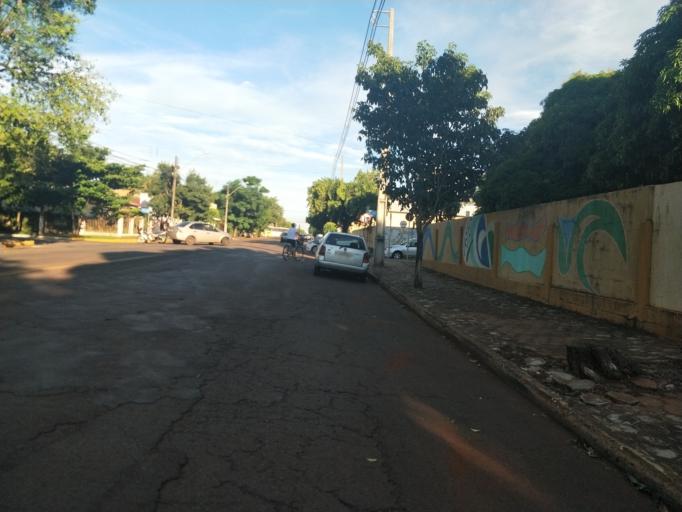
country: BR
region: Parana
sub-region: Marechal Candido Rondon
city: Marechal Candido Rondon
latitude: -24.5554
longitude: -54.0579
